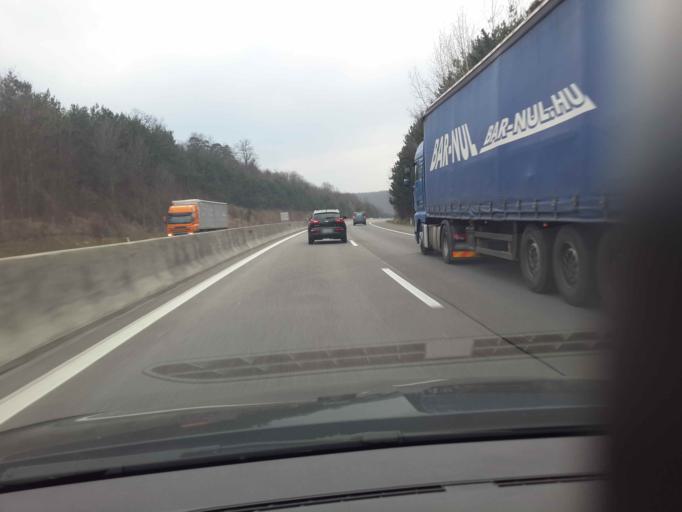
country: AT
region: Lower Austria
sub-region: Politischer Bezirk Modling
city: Gaaden
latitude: 48.0760
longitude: 16.2089
